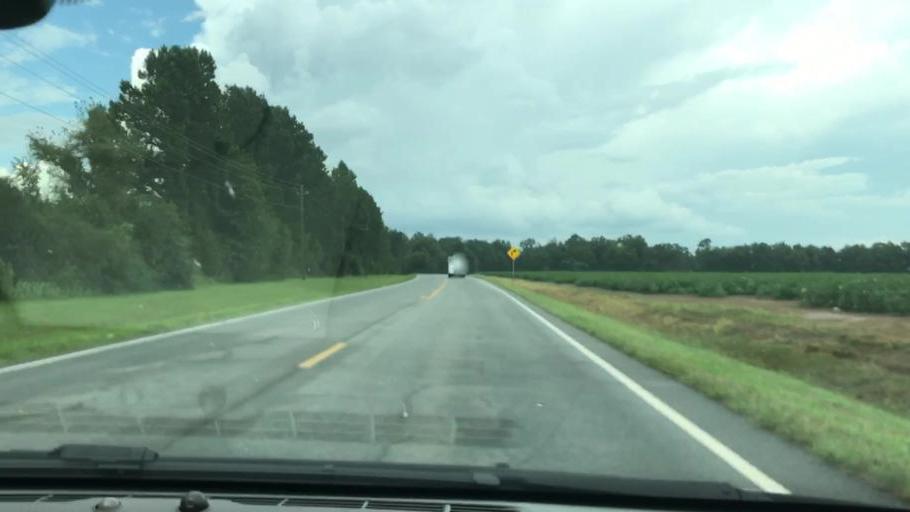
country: US
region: Georgia
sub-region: Early County
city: Blakely
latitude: 31.3839
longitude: -84.9574
